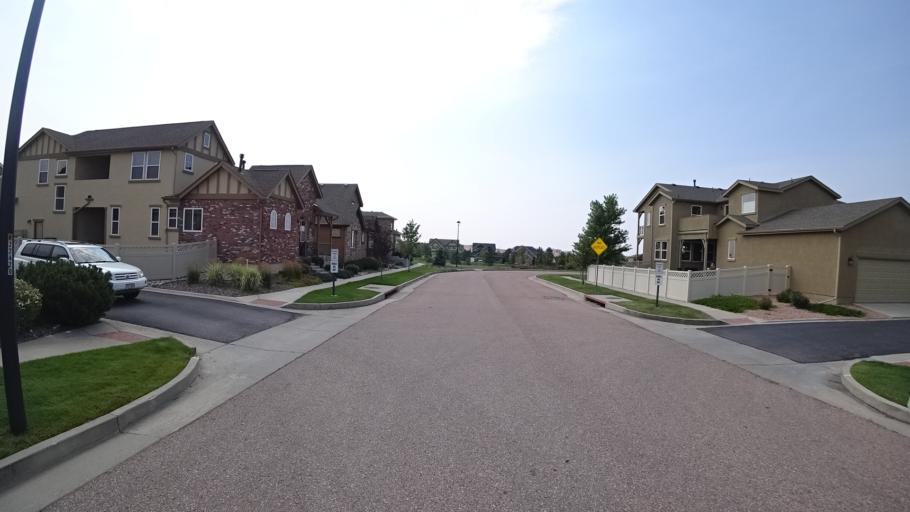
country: US
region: Colorado
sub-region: El Paso County
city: Black Forest
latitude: 38.9601
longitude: -104.7236
